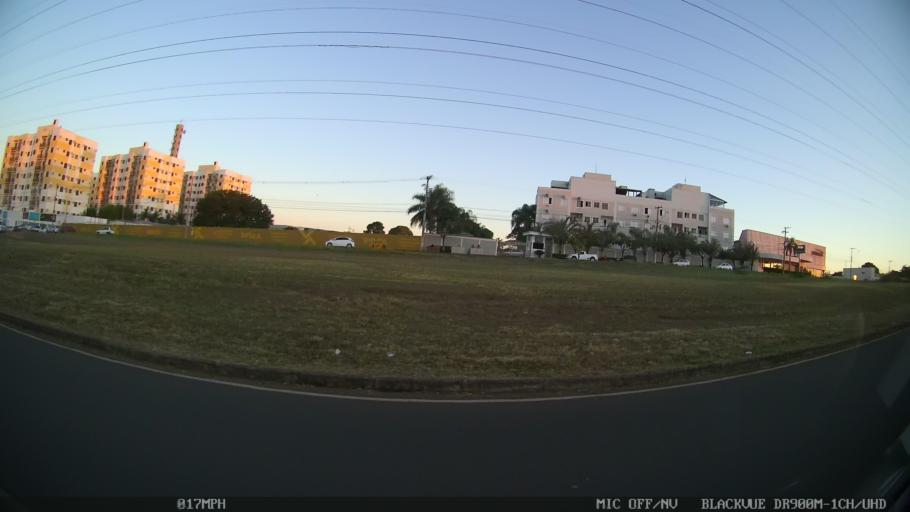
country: BR
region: Sao Paulo
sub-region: Sao Jose Do Rio Preto
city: Sao Jose do Rio Preto
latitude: -20.8440
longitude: -49.3880
